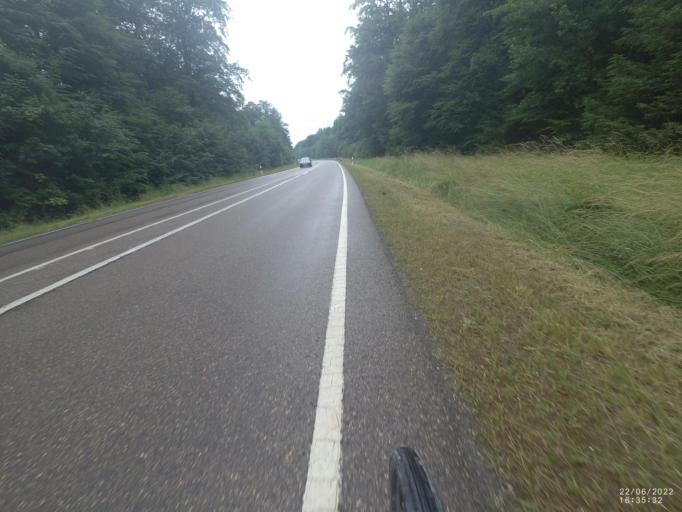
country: DE
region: Baden-Wuerttemberg
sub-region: Regierungsbezirk Stuttgart
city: Gerstetten
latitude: 48.6525
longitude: 10.0532
